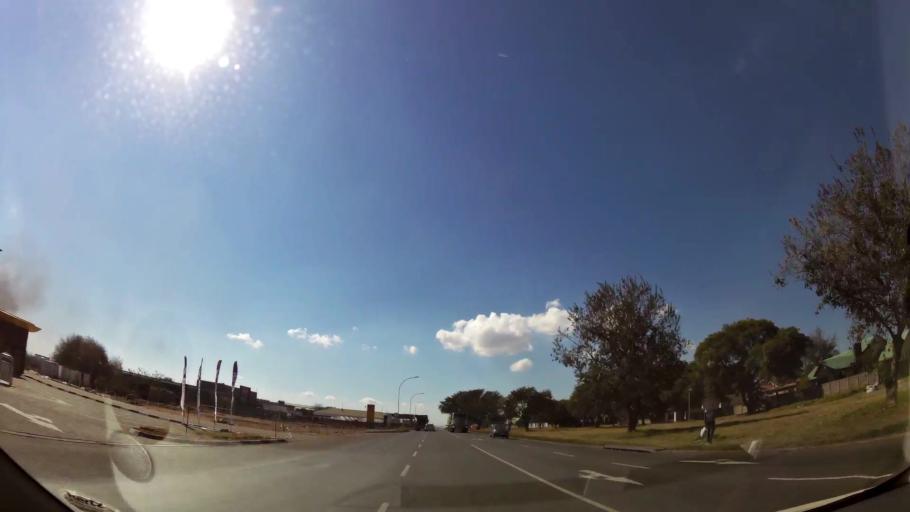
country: ZA
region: Mpumalanga
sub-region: Nkangala District Municipality
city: Witbank
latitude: -25.8652
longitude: 29.2199
